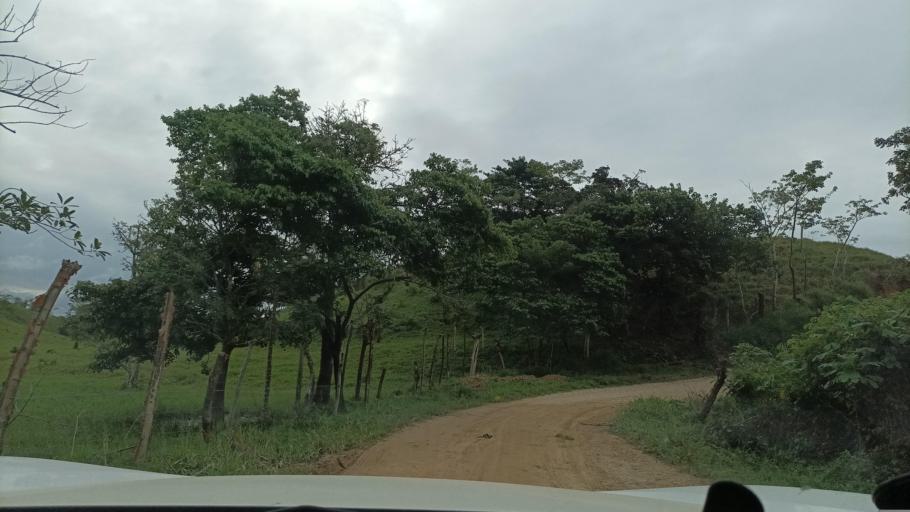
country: MX
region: Veracruz
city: Hidalgotitlan
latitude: 17.6017
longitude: -94.4228
